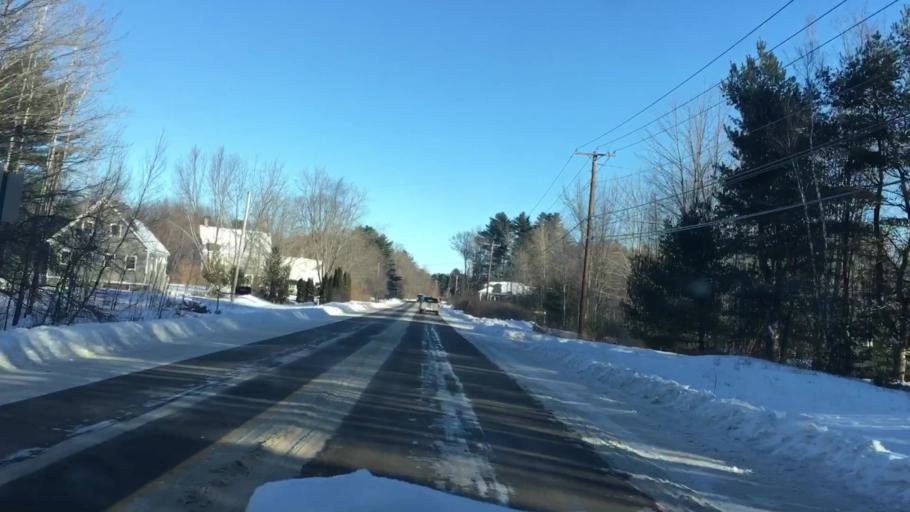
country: US
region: Maine
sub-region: Cumberland County
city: Brunswick
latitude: 43.9430
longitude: -69.9296
